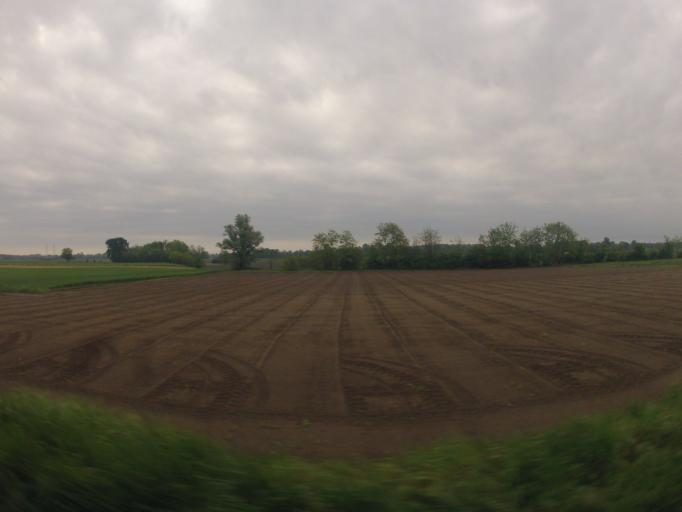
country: IT
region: Piedmont
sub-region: Provincia di Torino
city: Carignano
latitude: 44.8783
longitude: 7.6643
